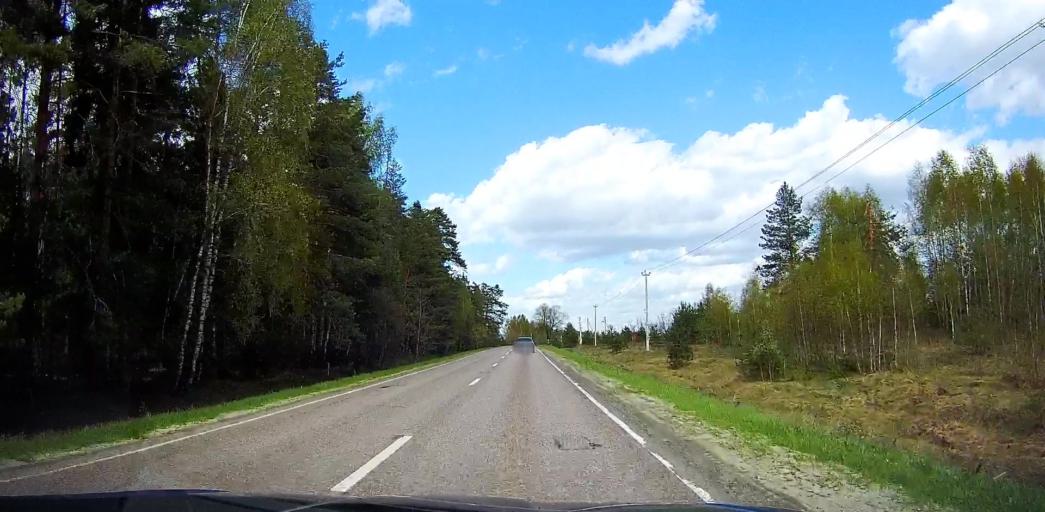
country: RU
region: Moskovskaya
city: Davydovo
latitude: 55.5969
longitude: 38.8388
